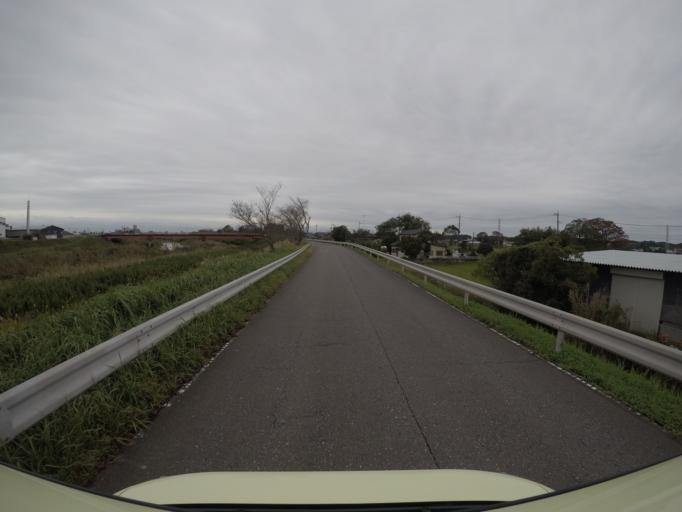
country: JP
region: Ibaraki
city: Naka
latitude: 36.0917
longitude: 140.1724
